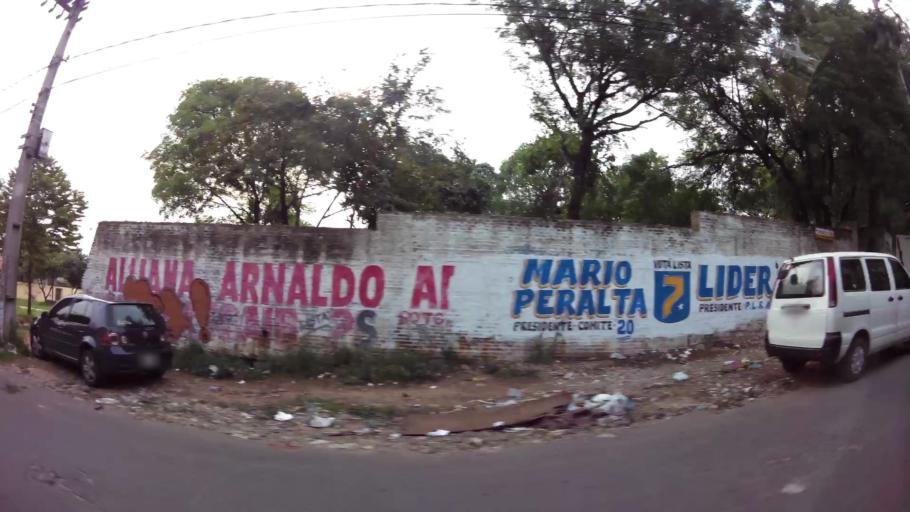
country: PY
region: Asuncion
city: Asuncion
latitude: -25.3043
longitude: -57.6171
